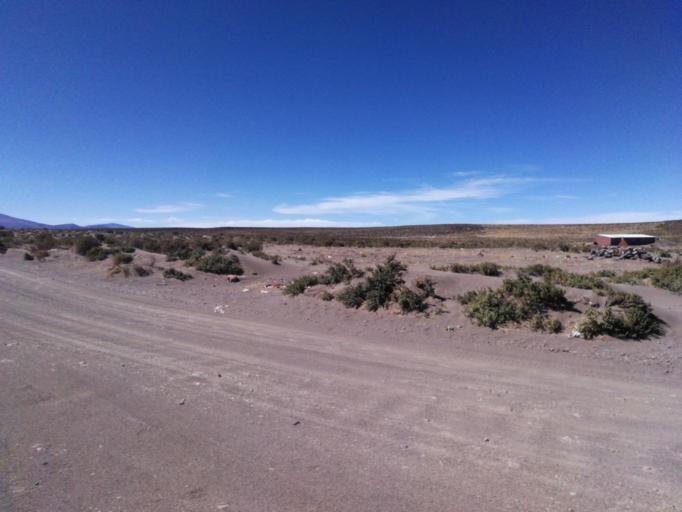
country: BO
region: Oruro
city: Cruz de Machacamarca
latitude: -19.2737
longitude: -68.2814
